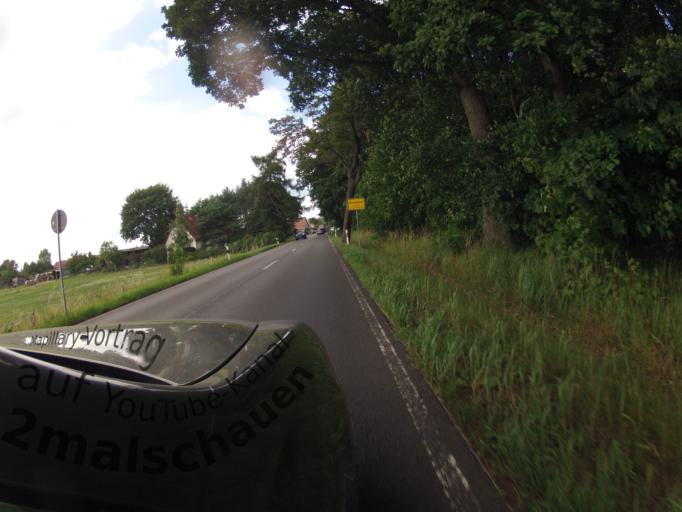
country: DE
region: Mecklenburg-Vorpommern
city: Seebad Heringsdorf
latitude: 53.9097
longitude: 14.1499
